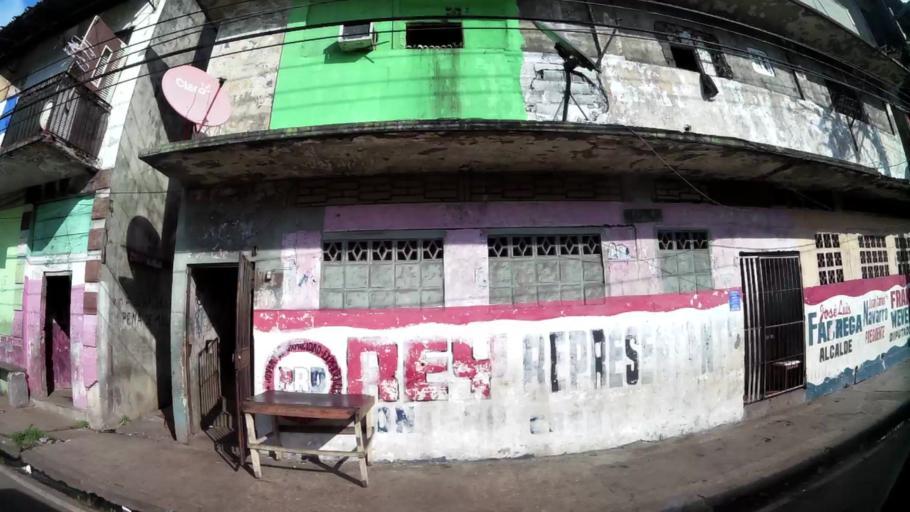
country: PA
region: Panama
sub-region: Distrito de Panama
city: Ancon
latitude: 8.9514
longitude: -79.5425
